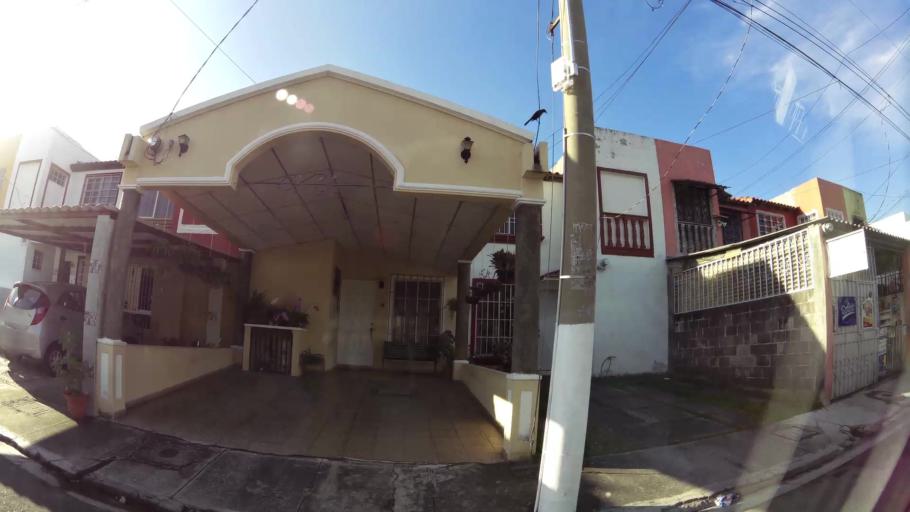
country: SV
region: La Libertad
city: Santa Tecla
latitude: 13.6858
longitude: -89.2837
